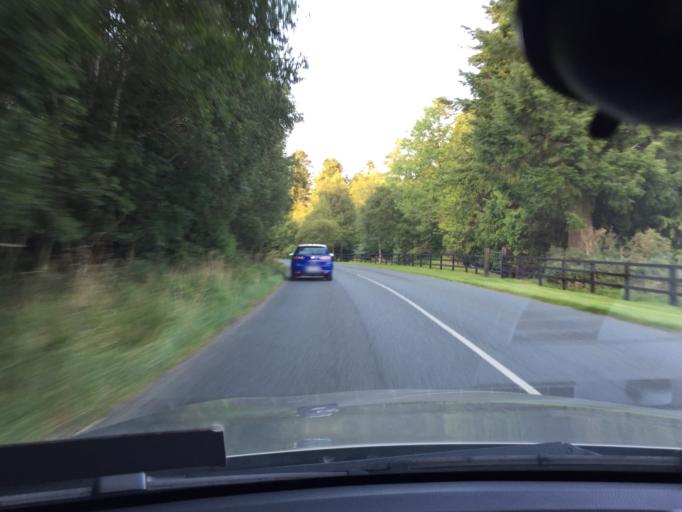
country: IE
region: Leinster
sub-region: Wicklow
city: Rathdrum
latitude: 53.0239
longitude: -6.2694
